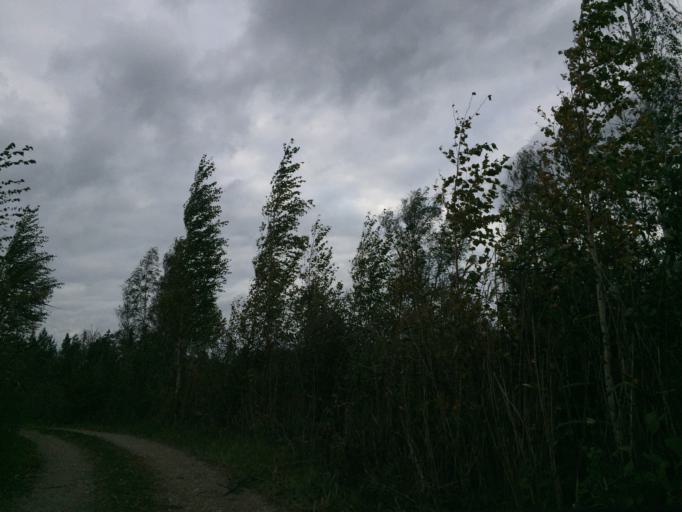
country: LV
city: Tireli
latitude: 56.8988
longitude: 23.5166
